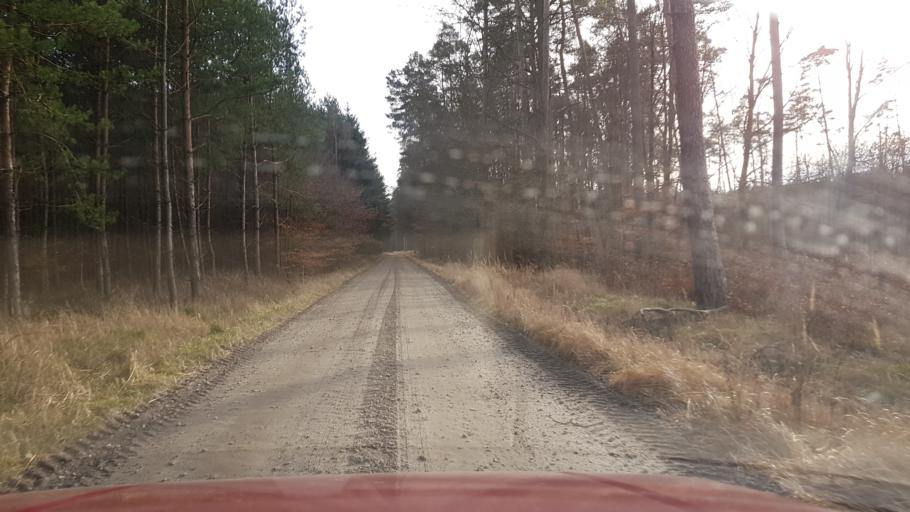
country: PL
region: West Pomeranian Voivodeship
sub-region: Powiat choszczenski
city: Pelczyce
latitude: 52.9234
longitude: 15.3681
